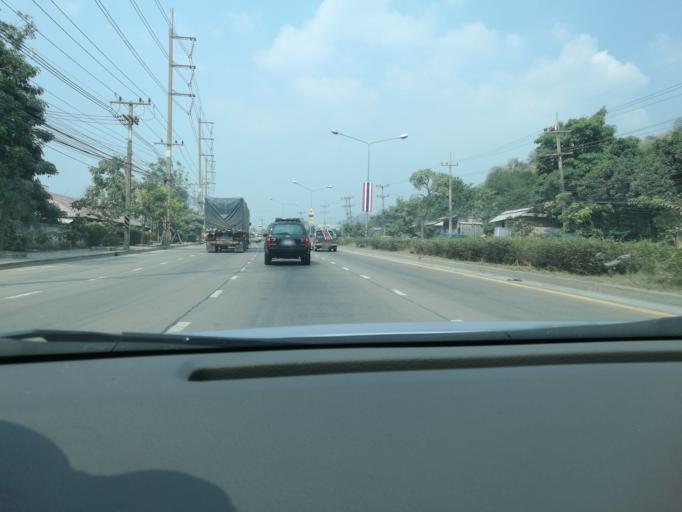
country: TH
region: Sara Buri
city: Phra Phutthabat
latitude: 14.6964
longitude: 100.8658
